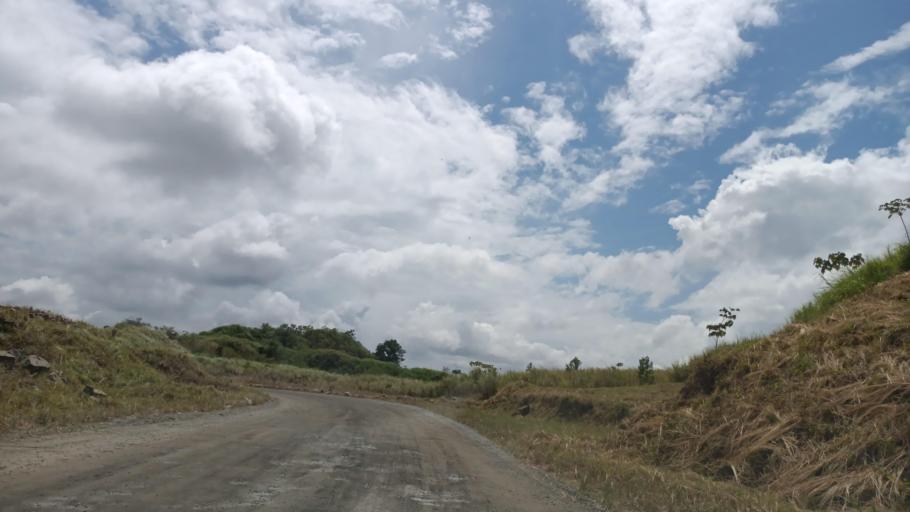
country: PA
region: Panama
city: Las Cumbres
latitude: 9.1069
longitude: -79.5000
